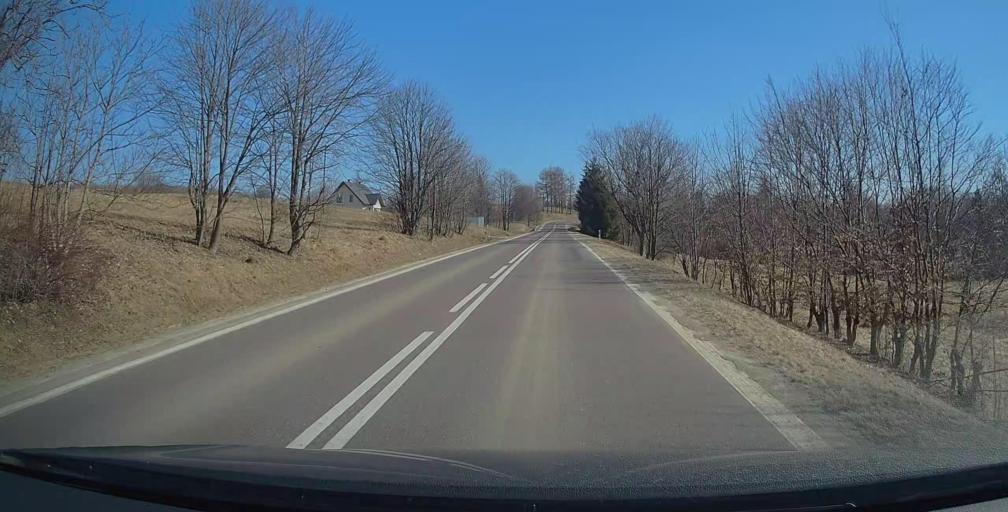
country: PL
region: Subcarpathian Voivodeship
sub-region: Powiat sanocki
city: Tyrawa Woloska
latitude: 49.6065
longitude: 22.4513
